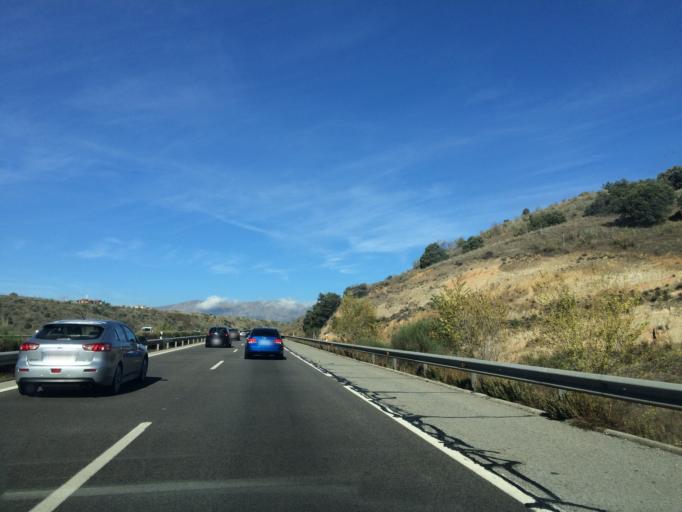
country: ES
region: Madrid
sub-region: Provincia de Madrid
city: Venturada
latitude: 40.8029
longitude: -3.6171
